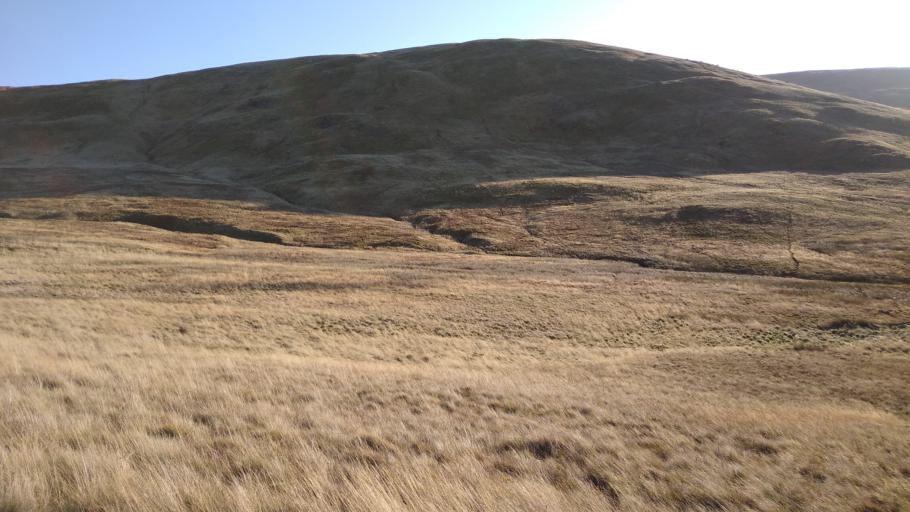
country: GB
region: England
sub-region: Cumbria
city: Windermere
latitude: 54.4998
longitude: -2.7957
